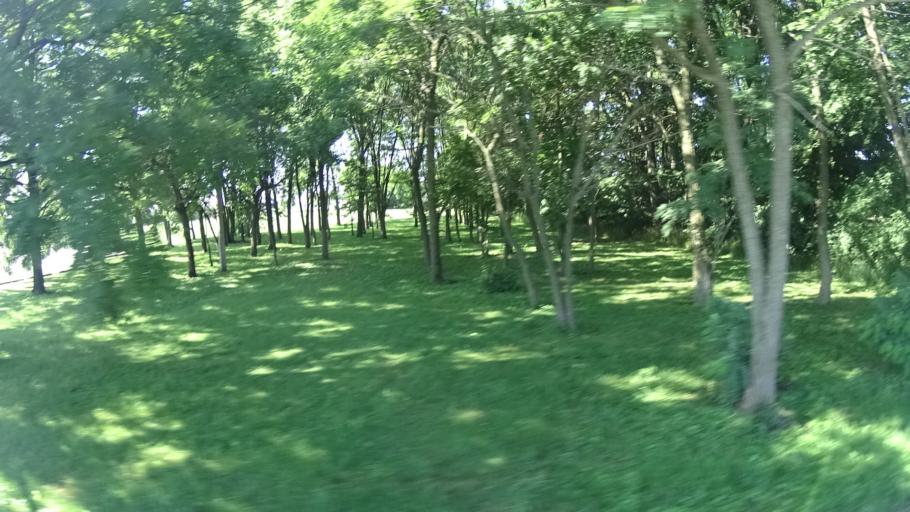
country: US
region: Indiana
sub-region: Madison County
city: Ingalls
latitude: 39.9740
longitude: -85.7743
